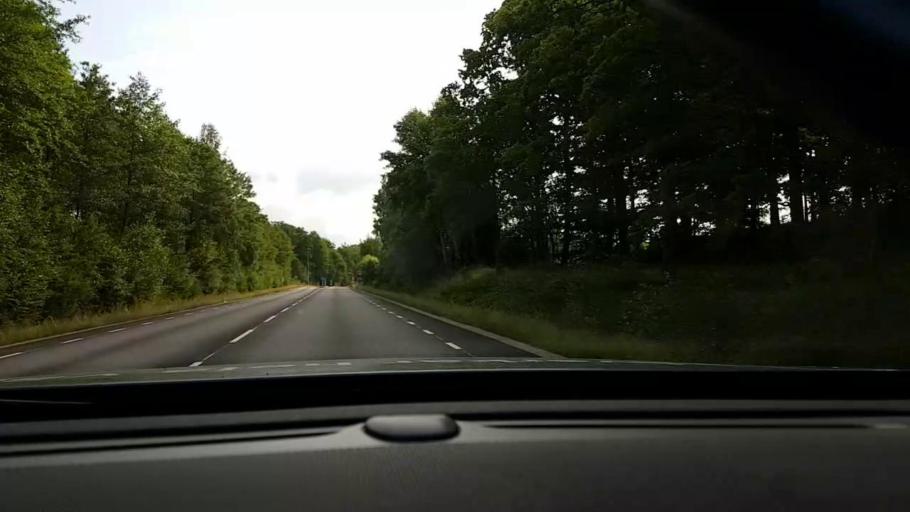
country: SE
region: Skane
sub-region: Hassleholms Kommun
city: Hassleholm
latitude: 56.1666
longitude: 13.7359
